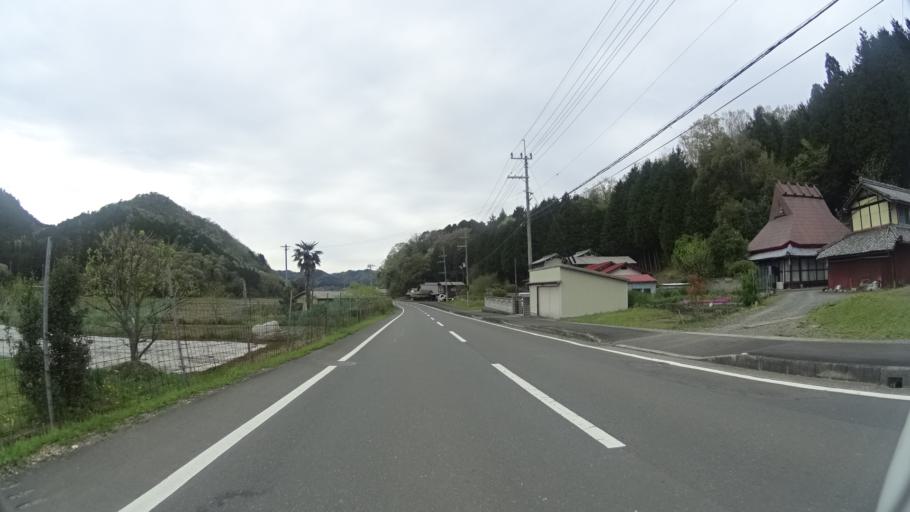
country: JP
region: Kyoto
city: Ayabe
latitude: 35.1806
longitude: 135.4367
